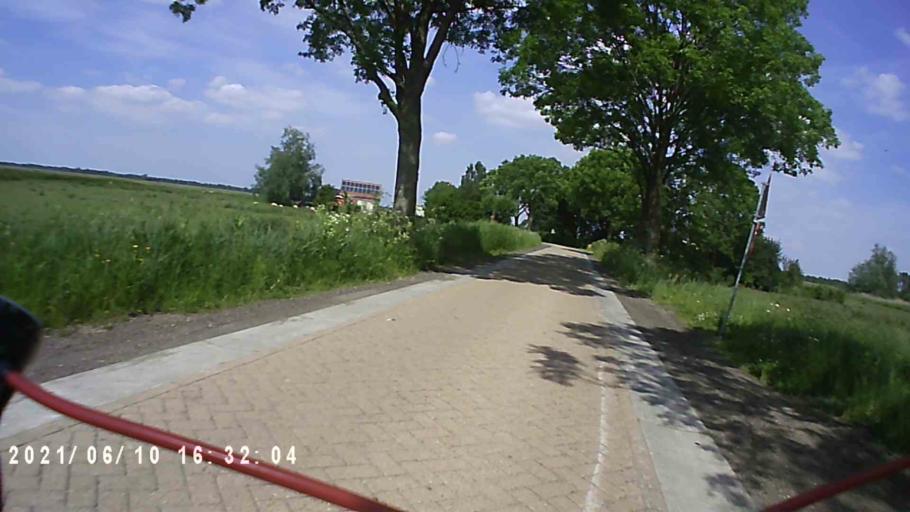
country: NL
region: Friesland
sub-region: Gemeente Achtkarspelen
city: Buitenpost
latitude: 53.2296
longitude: 6.1290
